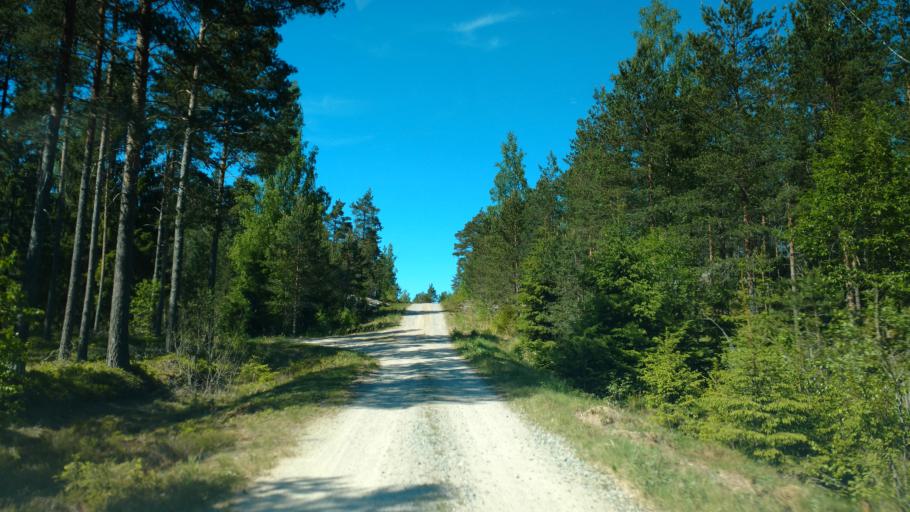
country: FI
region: Varsinais-Suomi
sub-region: Salo
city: Halikko
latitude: 60.4381
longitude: 22.9704
